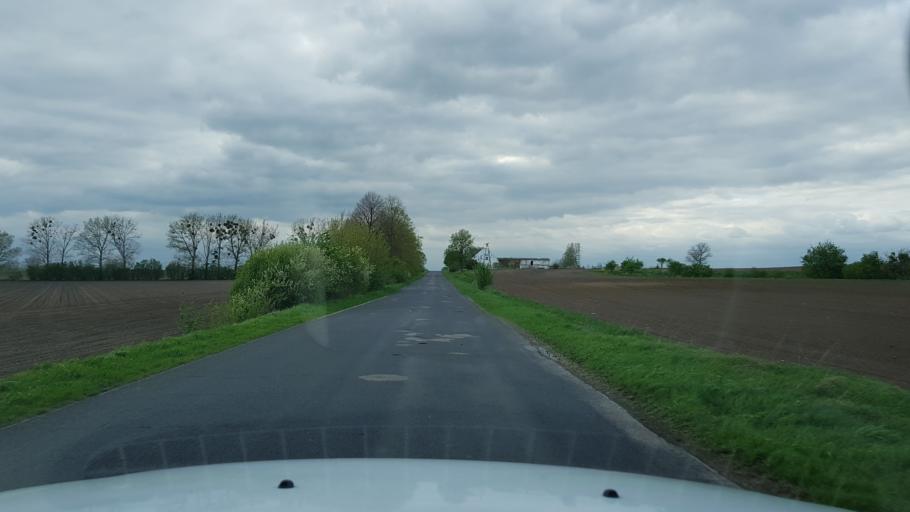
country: PL
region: West Pomeranian Voivodeship
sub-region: Powiat pyrzycki
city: Przelewice
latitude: 53.1407
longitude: 15.0263
